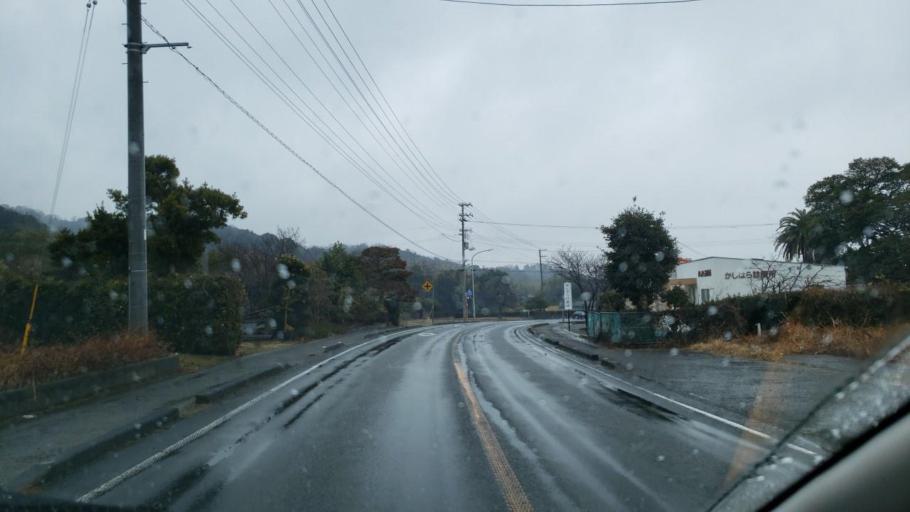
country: JP
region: Tokushima
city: Tokushima-shi
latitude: 34.1566
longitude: 134.5141
